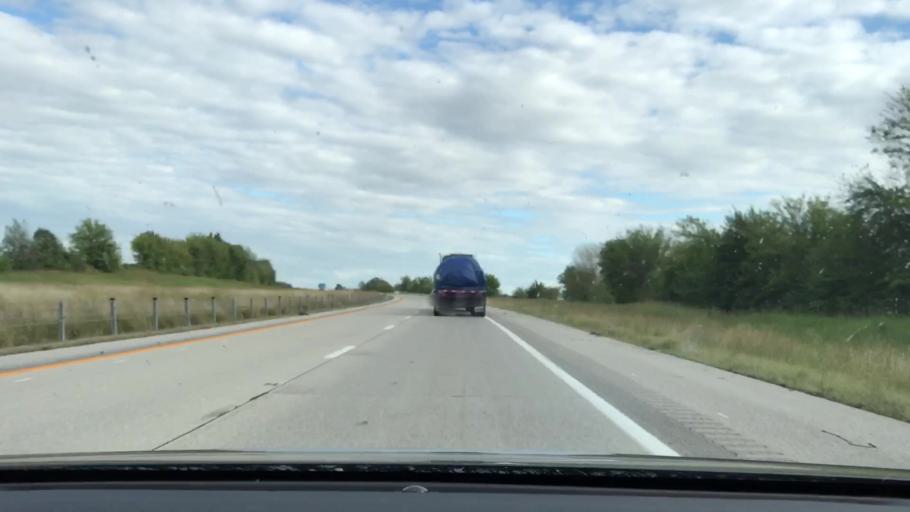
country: US
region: Kentucky
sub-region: Christian County
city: Hopkinsville
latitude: 36.7947
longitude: -87.6026
